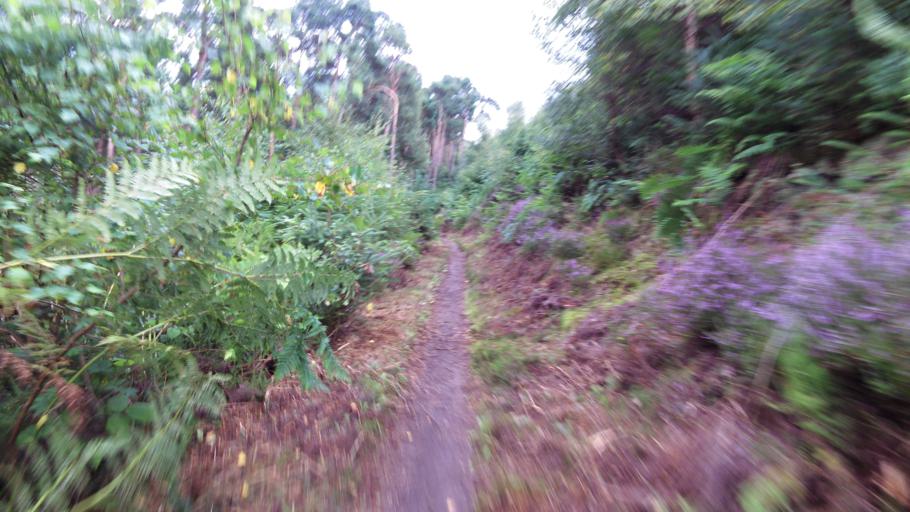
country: GB
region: England
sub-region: North Yorkshire
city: Thornton Dale
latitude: 54.2910
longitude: -0.6800
